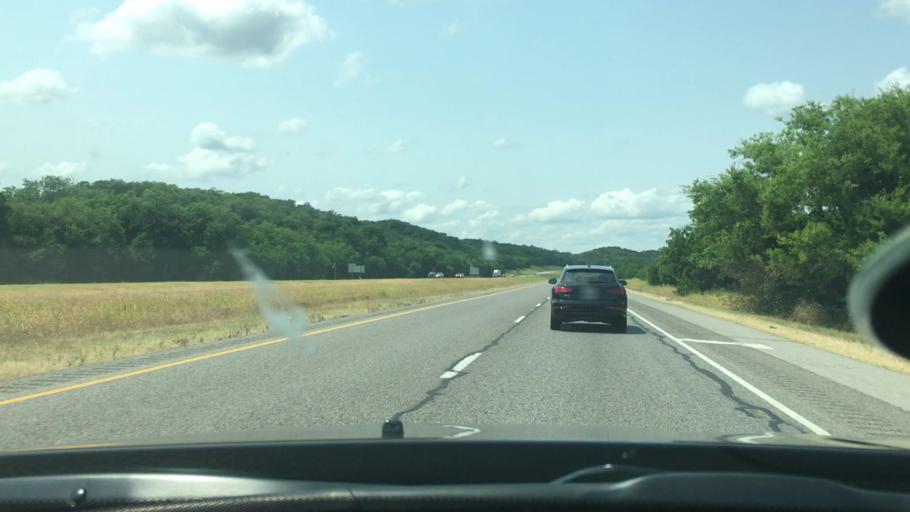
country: US
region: Oklahoma
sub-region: Murray County
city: Davis
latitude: 34.4610
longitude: -97.1450
